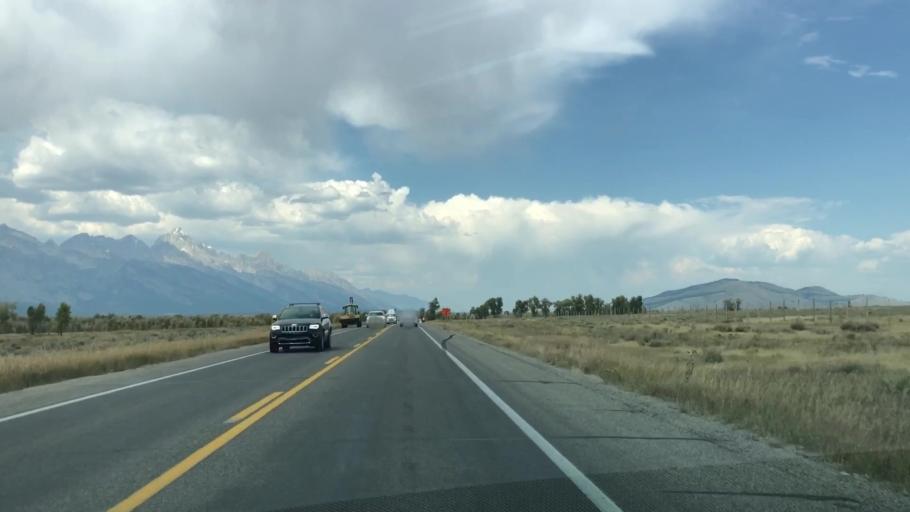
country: US
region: Wyoming
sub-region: Teton County
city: Jackson
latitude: 43.5555
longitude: -110.7325
